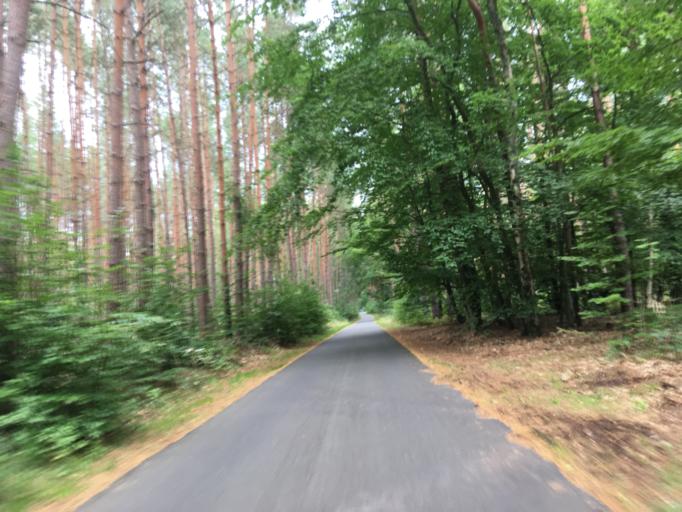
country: DE
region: Brandenburg
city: Joachimsthal
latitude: 53.0133
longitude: 13.7389
